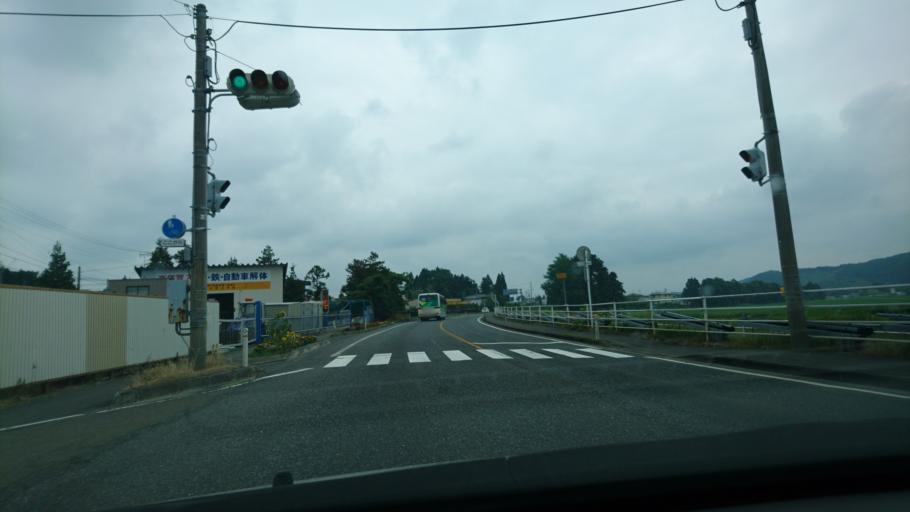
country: JP
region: Miyagi
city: Furukawa
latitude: 38.7131
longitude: 140.8295
